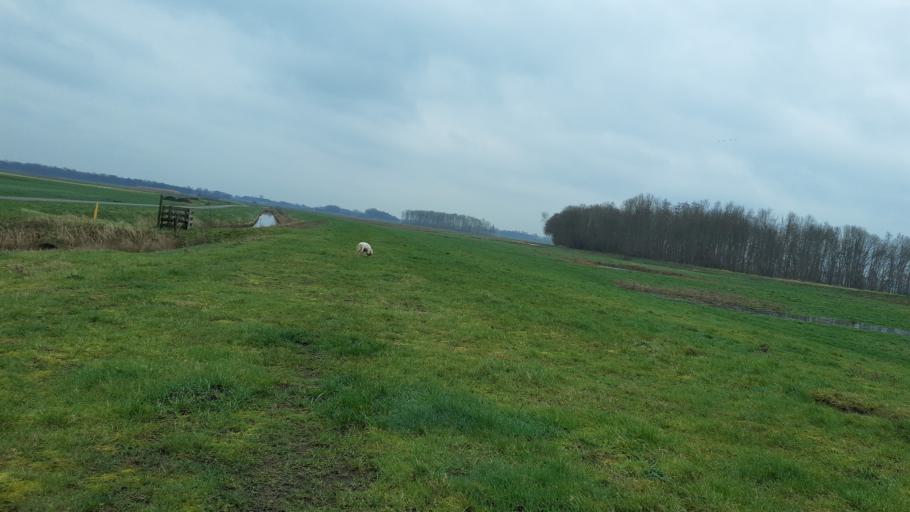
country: NL
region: Drenthe
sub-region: Gemeente Aa en Hunze
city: Anloo
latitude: 53.0448
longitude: 6.7953
